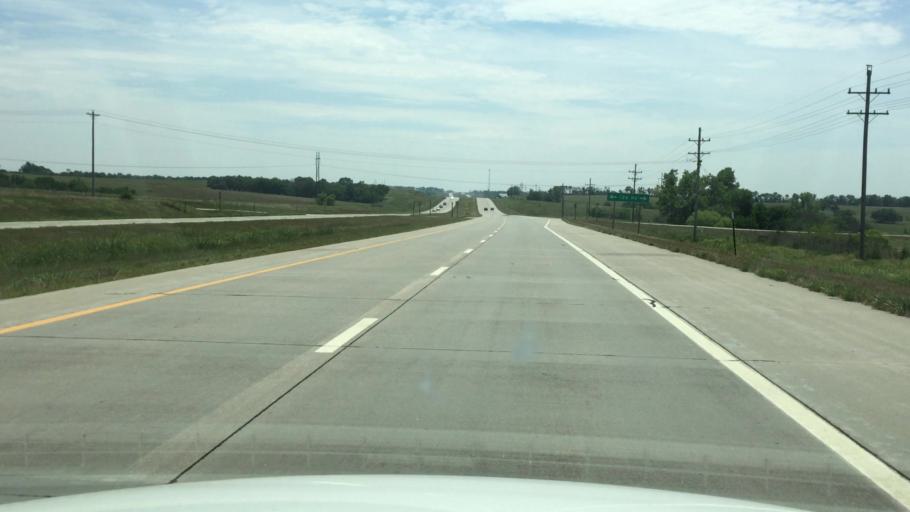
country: US
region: Kansas
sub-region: Jackson County
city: Holton
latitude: 39.2758
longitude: -95.7199
